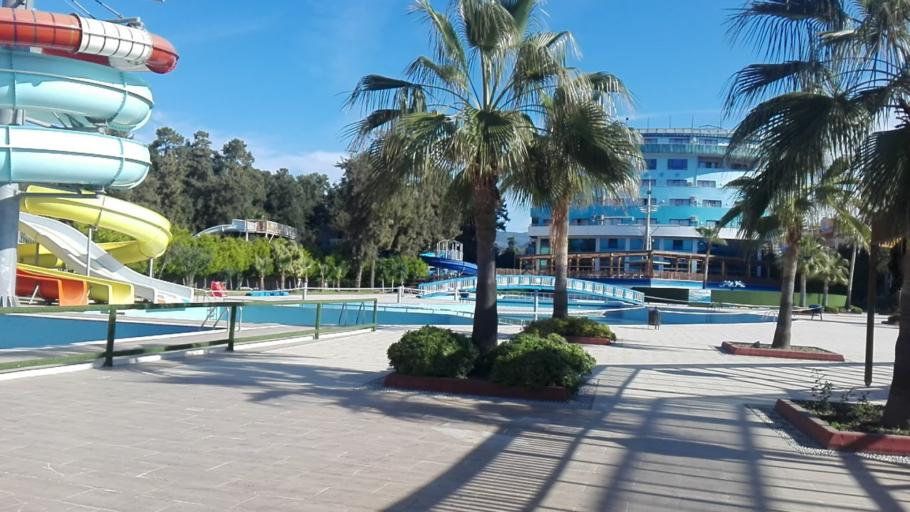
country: TR
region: Antalya
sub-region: Alanya
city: Payallar
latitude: 36.5786
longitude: 31.8846
